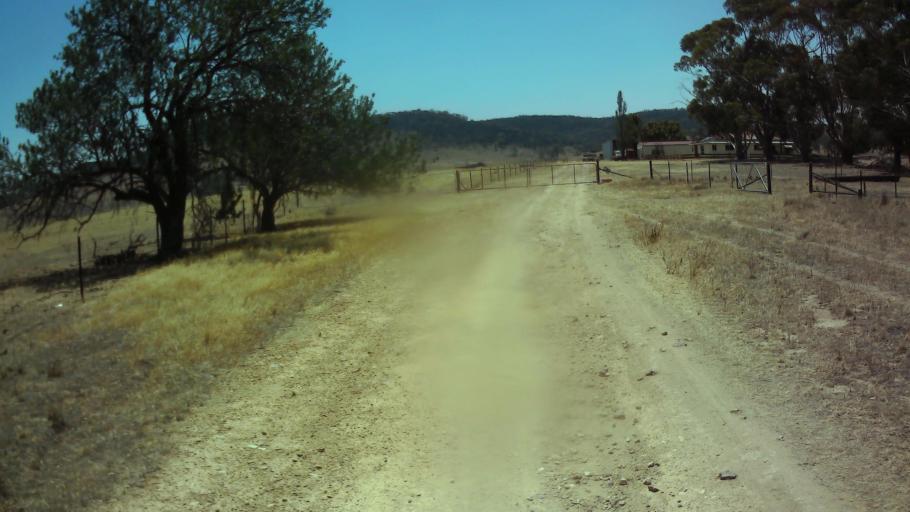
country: AU
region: New South Wales
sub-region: Weddin
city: Grenfell
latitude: -33.9122
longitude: 148.3219
